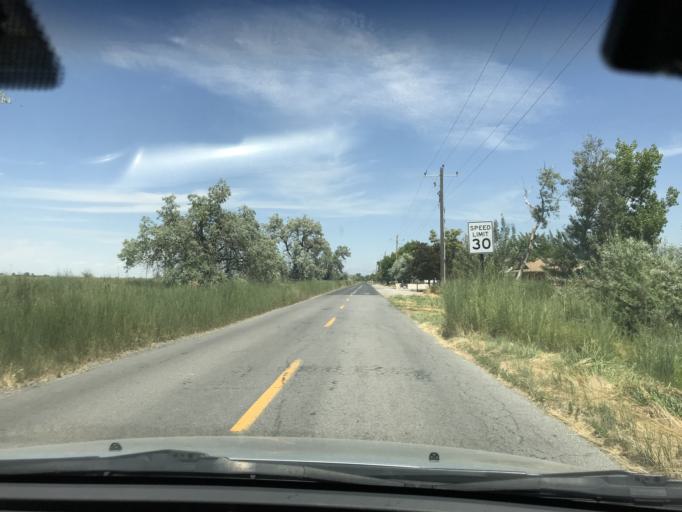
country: US
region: Utah
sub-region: Davis County
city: North Salt Lake
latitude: 40.8244
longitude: -111.9535
